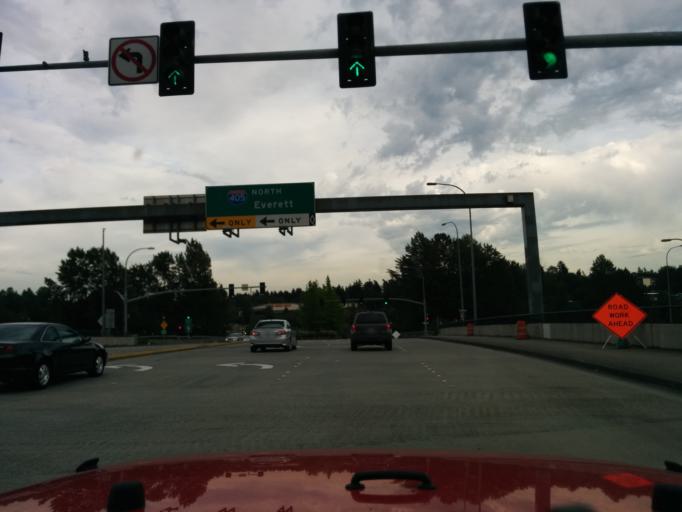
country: US
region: Washington
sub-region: King County
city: Bellevue
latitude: 47.6135
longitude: -122.1892
